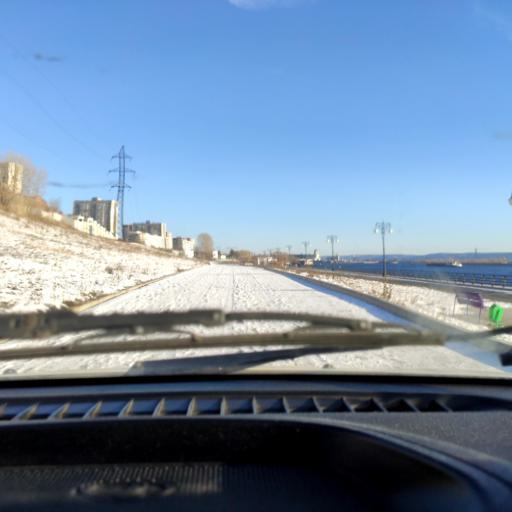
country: RU
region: Samara
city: Zhigulevsk
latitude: 53.4719
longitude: 49.4607
